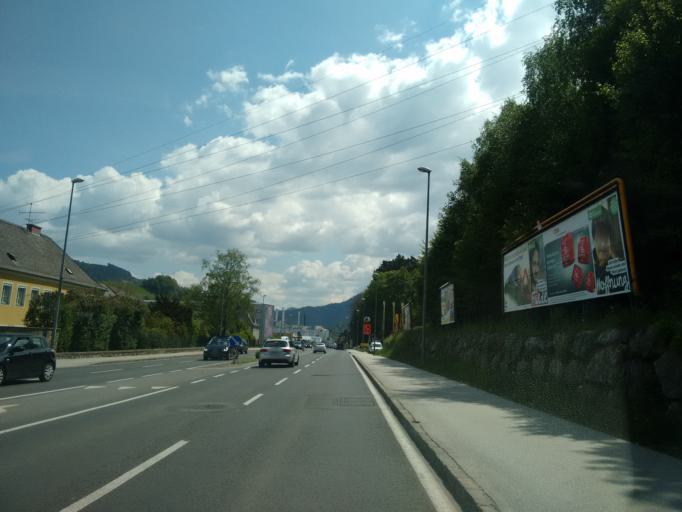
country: AT
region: Styria
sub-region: Politischer Bezirk Bruck-Muerzzuschlag
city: Bruck an der Mur
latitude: 47.4233
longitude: 15.2724
